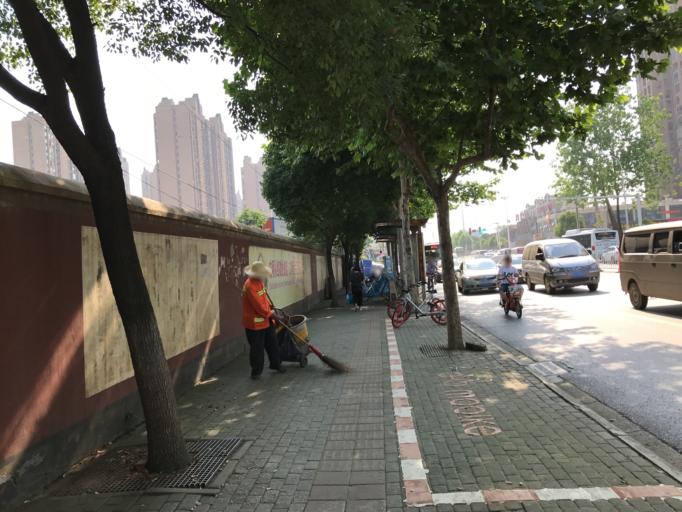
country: CN
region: Hubei
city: Shizishan
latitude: 30.4840
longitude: 114.3216
